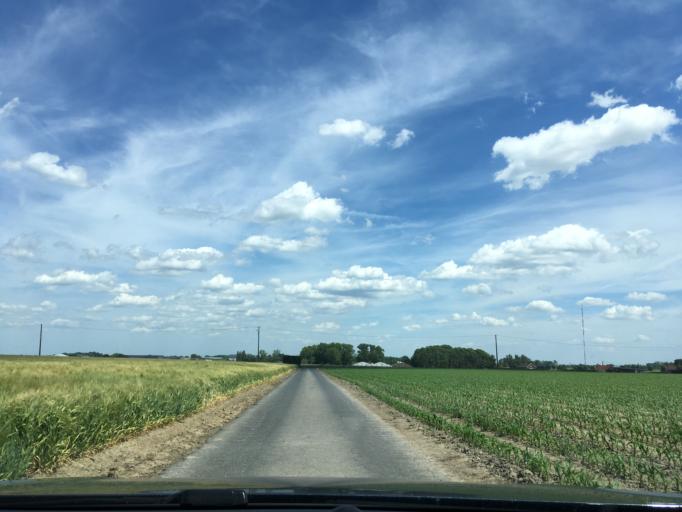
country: BE
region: Flanders
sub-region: Provincie West-Vlaanderen
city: Ardooie
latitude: 51.0085
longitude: 3.1985
